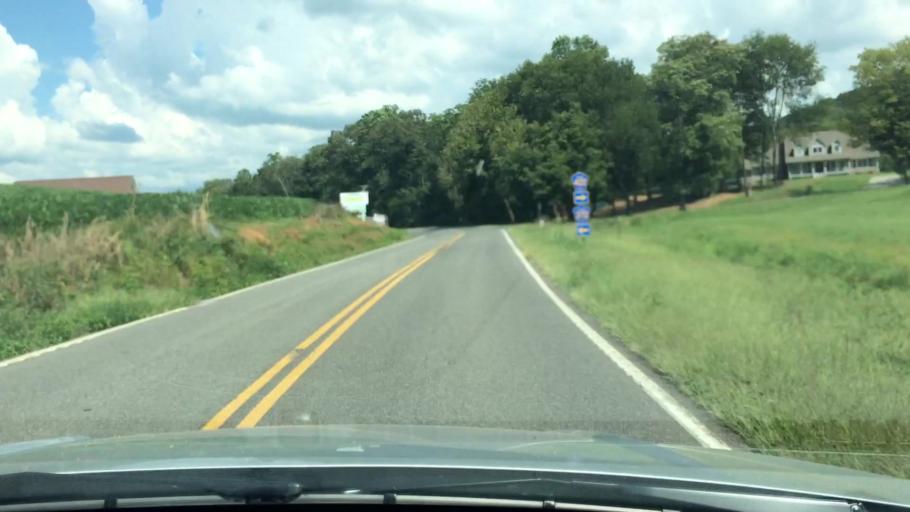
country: US
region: Tennessee
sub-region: McMinn County
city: Englewood
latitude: 35.4819
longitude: -84.5235
